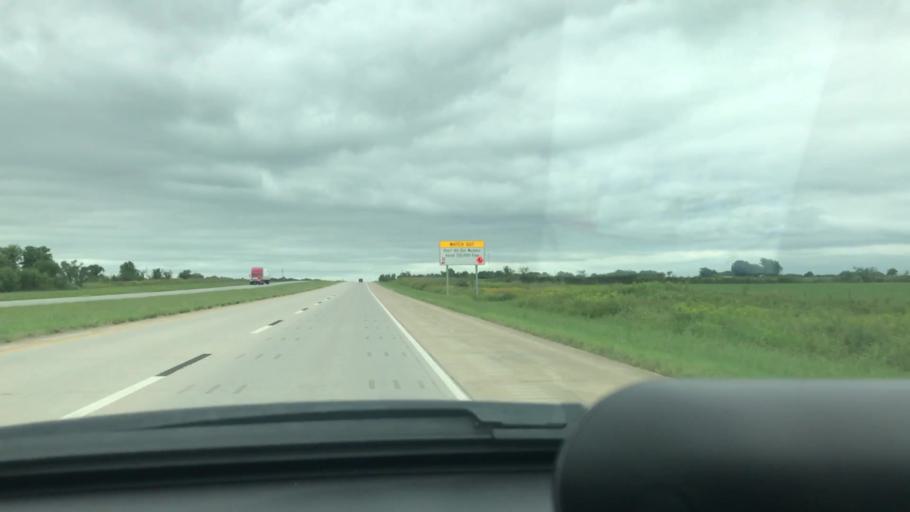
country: US
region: Oklahoma
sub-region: Mayes County
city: Chouteau
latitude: 36.0848
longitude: -95.3639
